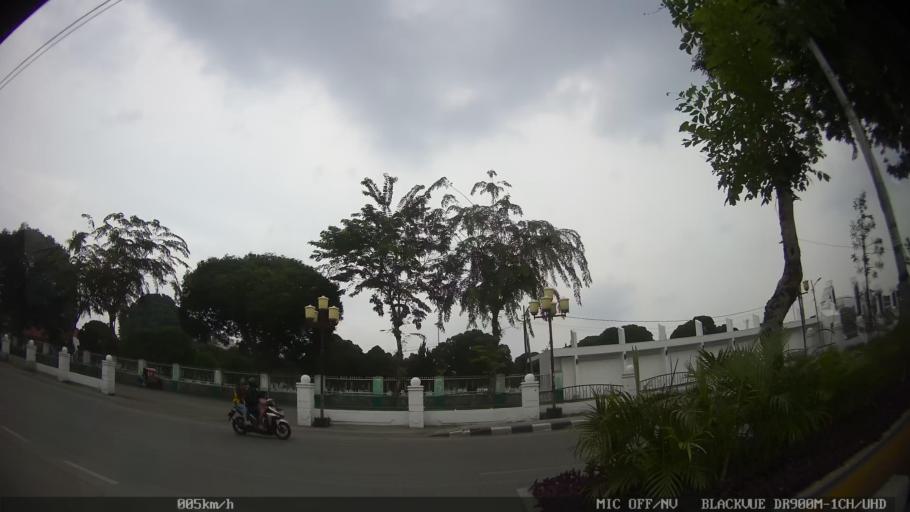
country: ID
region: North Sumatra
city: Medan
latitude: 3.5702
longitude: 98.6904
